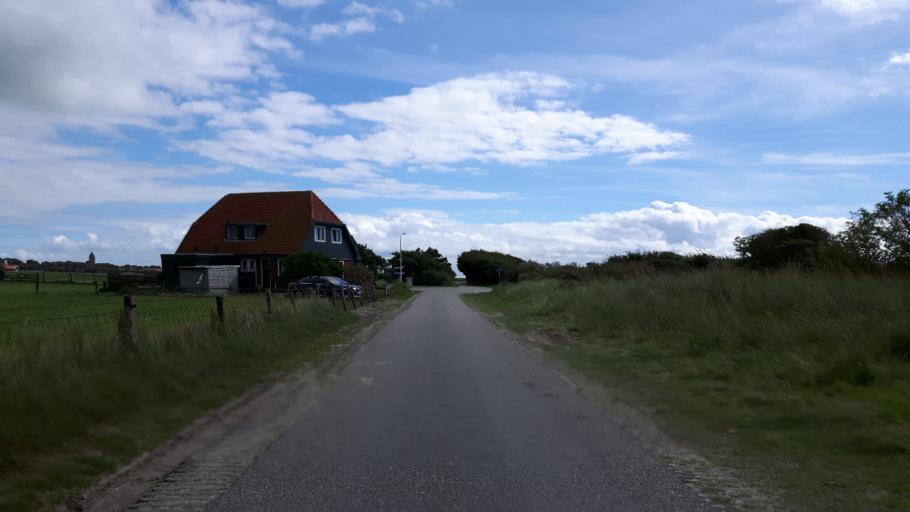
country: NL
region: Friesland
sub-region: Gemeente Ameland
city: Hollum
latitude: 53.4397
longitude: 5.6215
